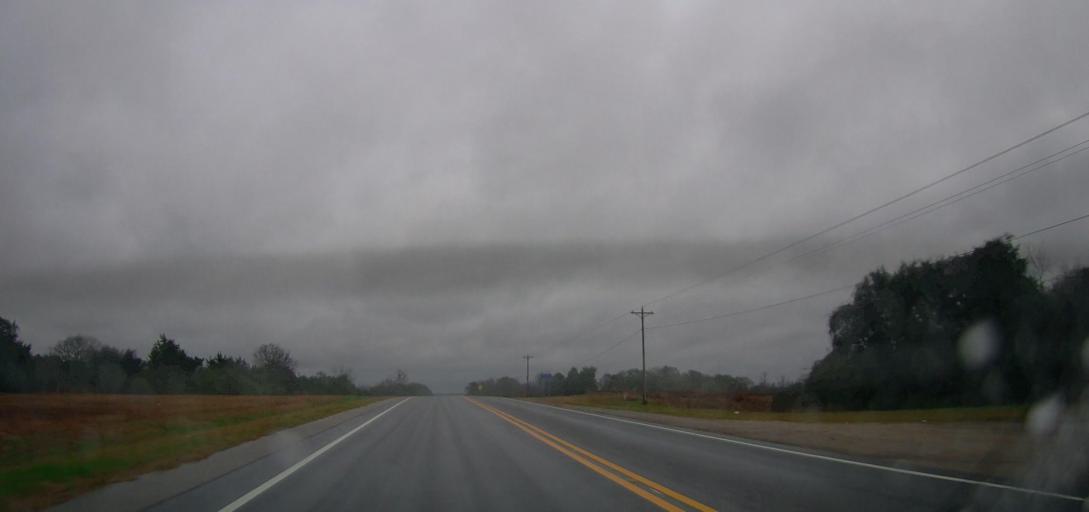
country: US
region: Alabama
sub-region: Chilton County
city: Thorsby
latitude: 32.7827
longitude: -86.8962
